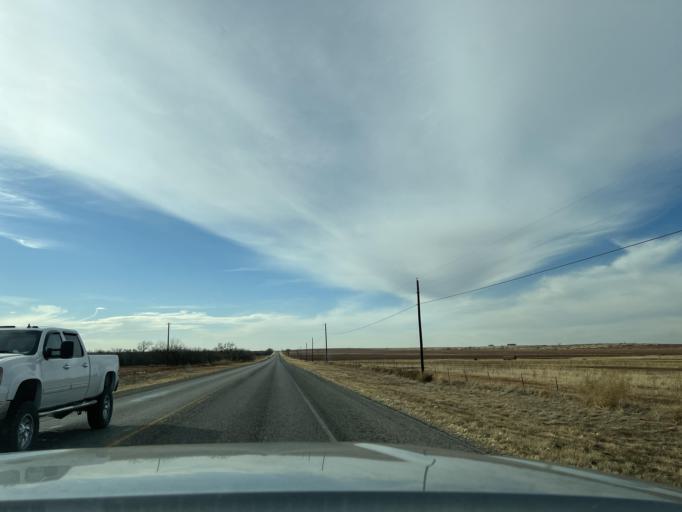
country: US
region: Texas
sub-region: Fisher County
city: Roby
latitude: 32.7411
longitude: -100.4701
